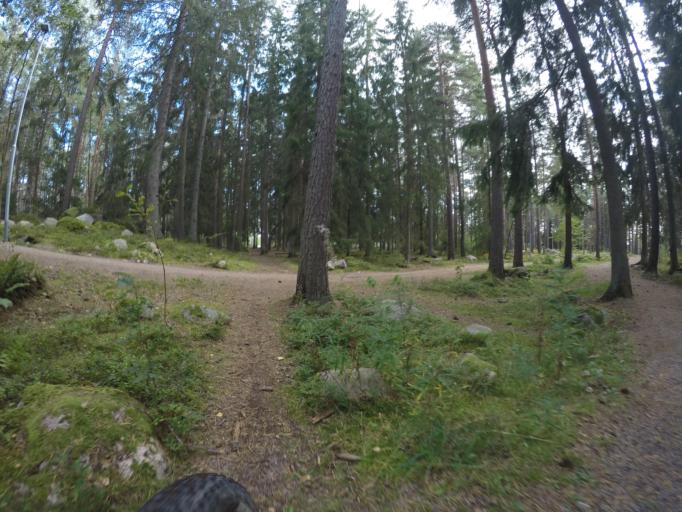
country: SE
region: Vaestmanland
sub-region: Kopings Kommun
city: Koping
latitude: 59.5285
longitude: 16.0009
